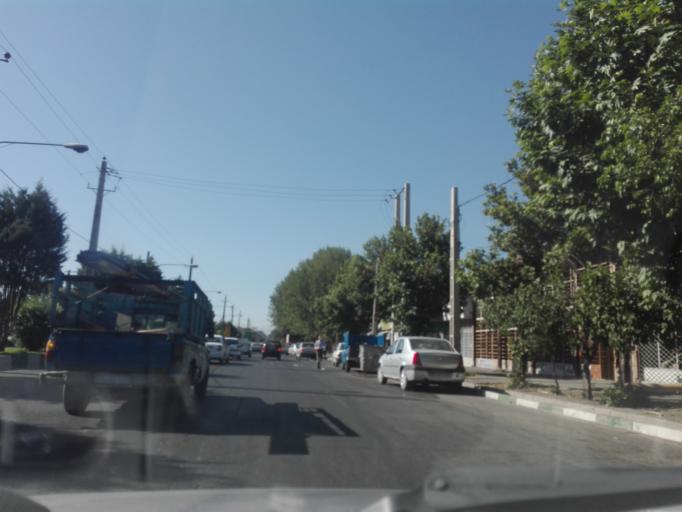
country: IR
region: Tehran
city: Shahriar
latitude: 35.6405
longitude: 51.0639
